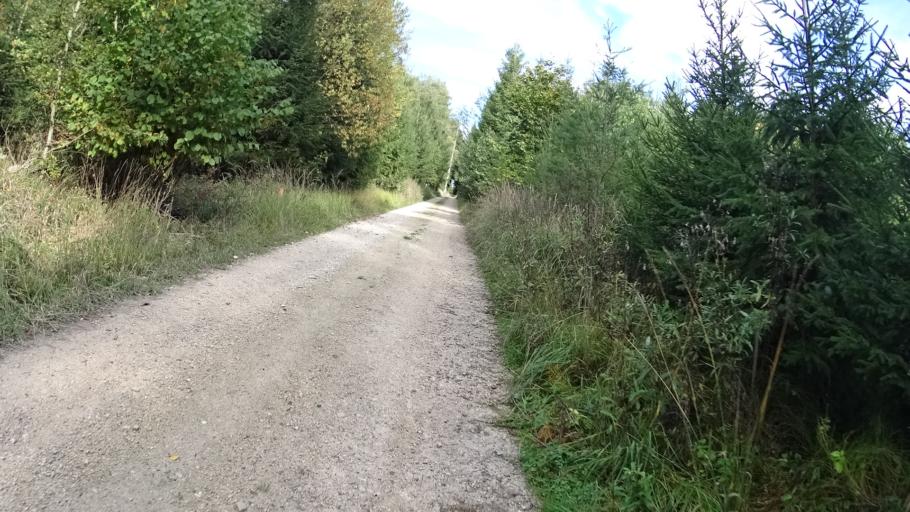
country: DE
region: Bavaria
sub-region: Upper Bavaria
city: Bohmfeld
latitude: 48.8737
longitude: 11.3800
